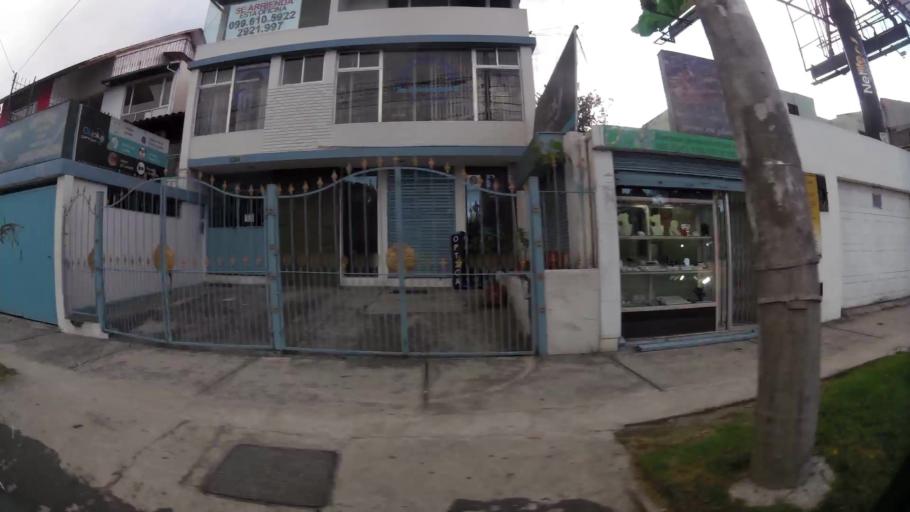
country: EC
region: Pichincha
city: Quito
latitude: -0.1878
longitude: -78.4878
